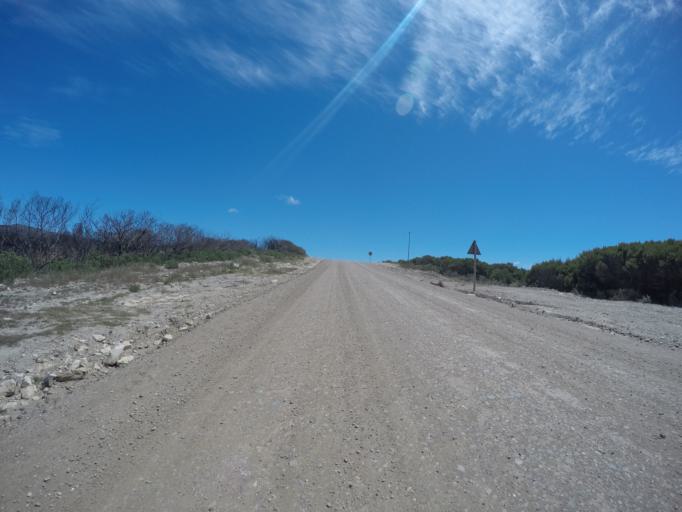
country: ZA
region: Western Cape
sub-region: Eden District Municipality
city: Riversdale
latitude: -34.4193
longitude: 20.8532
